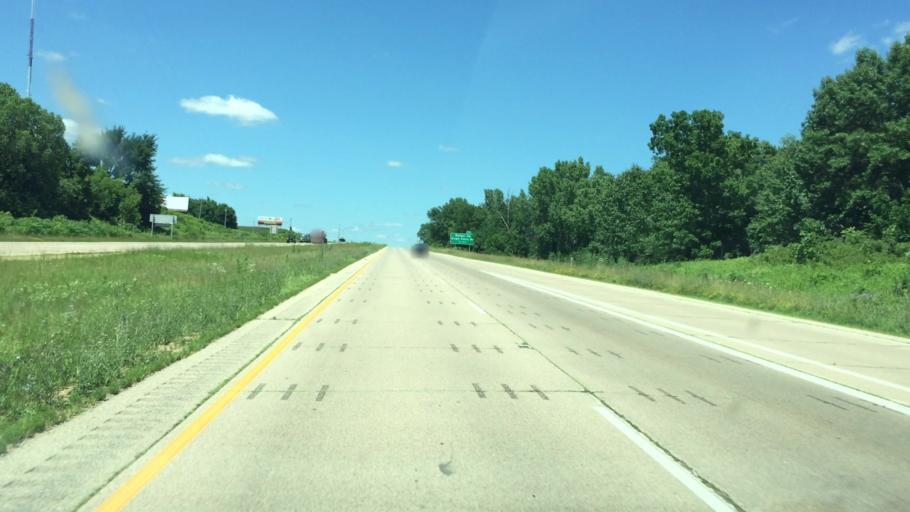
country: US
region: Illinois
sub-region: Jo Daviess County
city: East Dubuque
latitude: 42.5233
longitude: -90.6142
